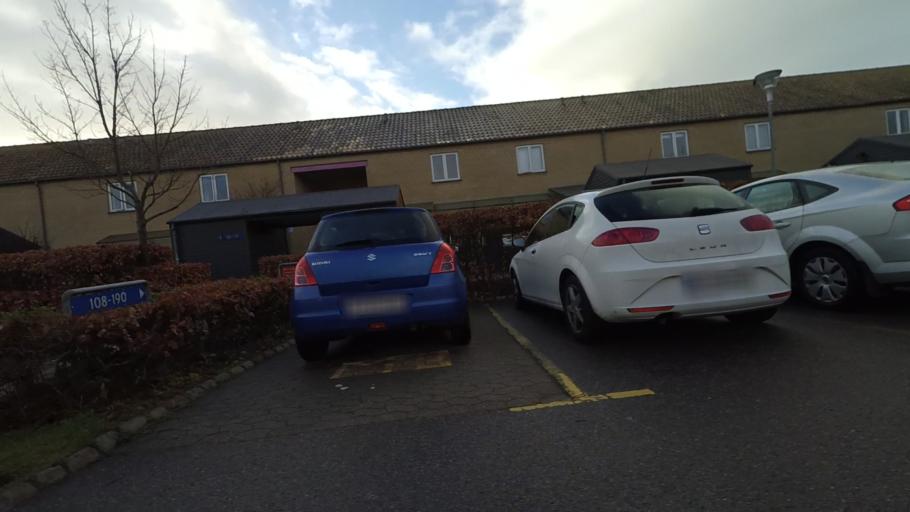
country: DK
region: Central Jutland
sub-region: Arhus Kommune
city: Marslet
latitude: 56.1026
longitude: 10.1680
